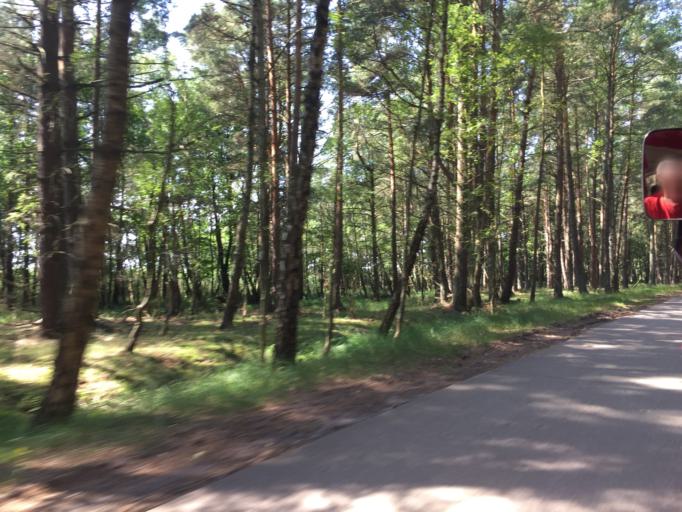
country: PL
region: Pomeranian Voivodeship
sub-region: Powiat leborski
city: Leba
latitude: 54.7538
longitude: 17.5041
